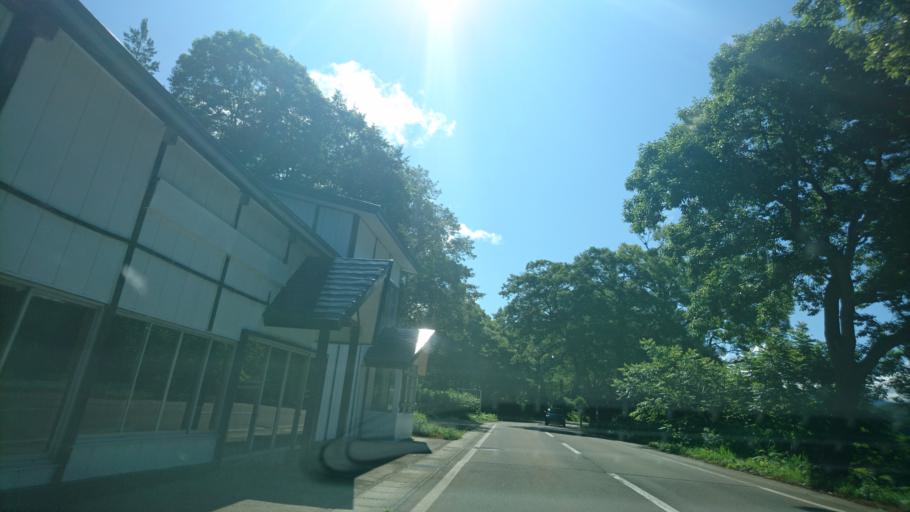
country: JP
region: Akita
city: Kakunodatemachi
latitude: 39.7394
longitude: 140.6917
